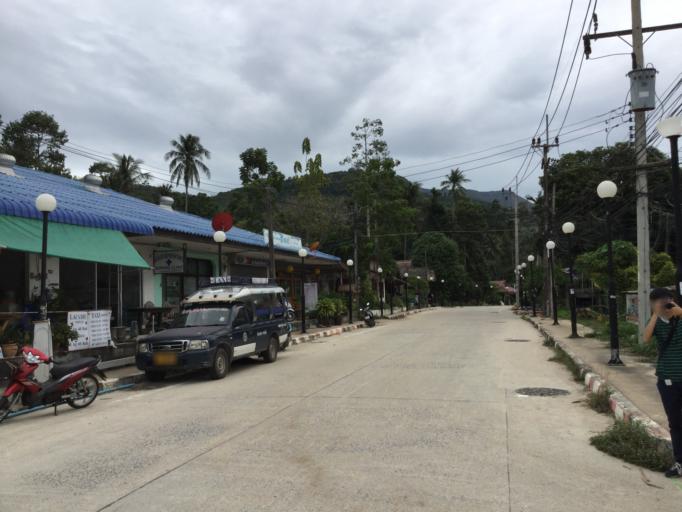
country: TH
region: Nakhon Si Thammarat
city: Ko Pha Ngan
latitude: 9.7692
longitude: 100.0564
